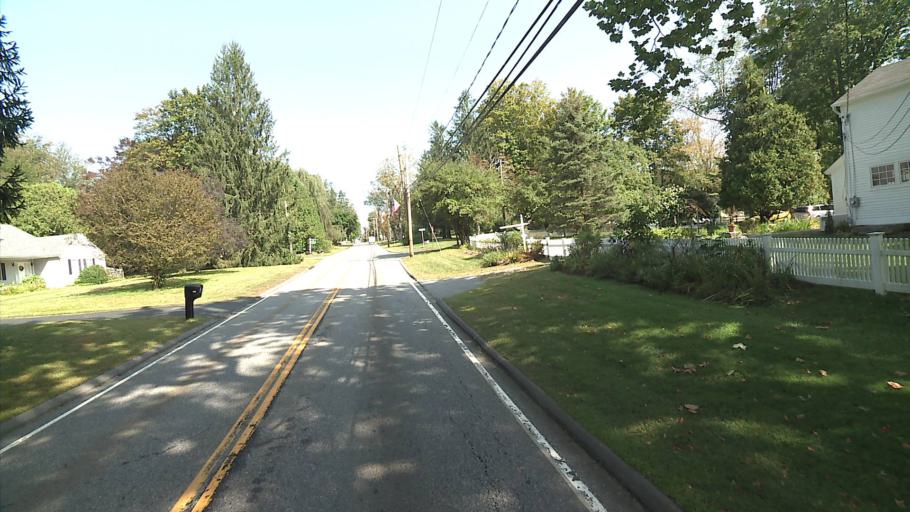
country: US
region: Connecticut
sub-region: Windham County
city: South Woodstock
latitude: 41.8806
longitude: -71.9618
